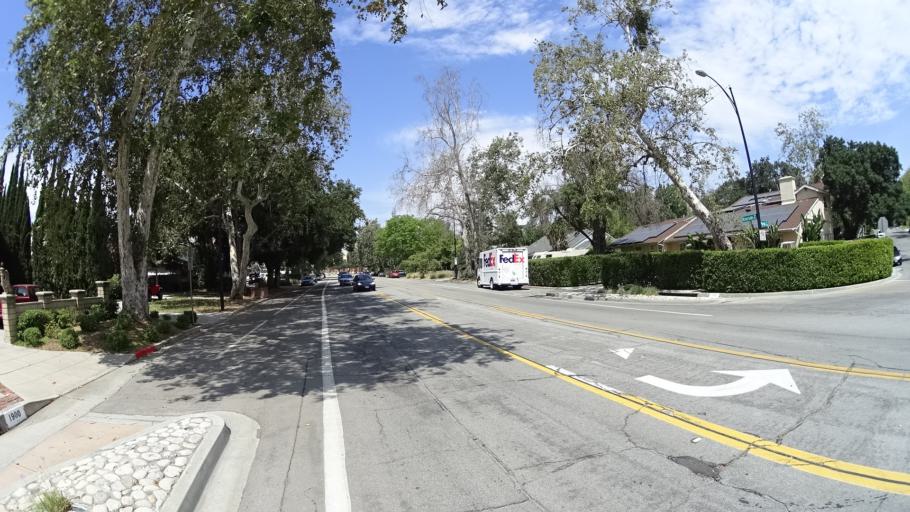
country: US
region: California
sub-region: Los Angeles County
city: Burbank
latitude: 34.1565
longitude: -118.3202
